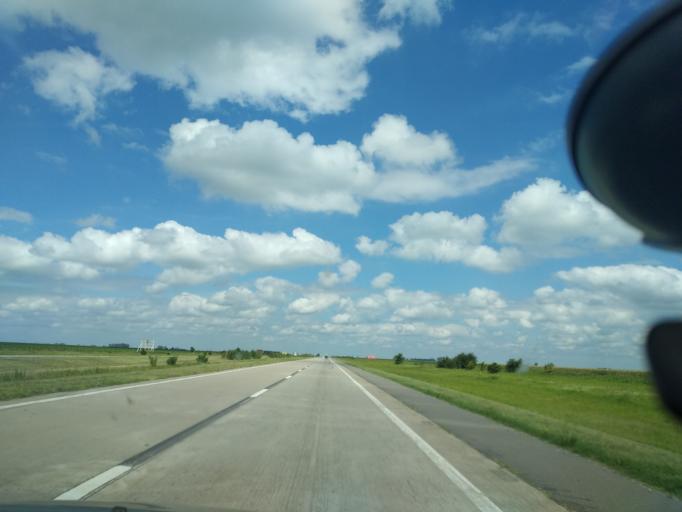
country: AR
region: Cordoba
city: Leones
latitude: -32.6061
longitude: -62.4266
